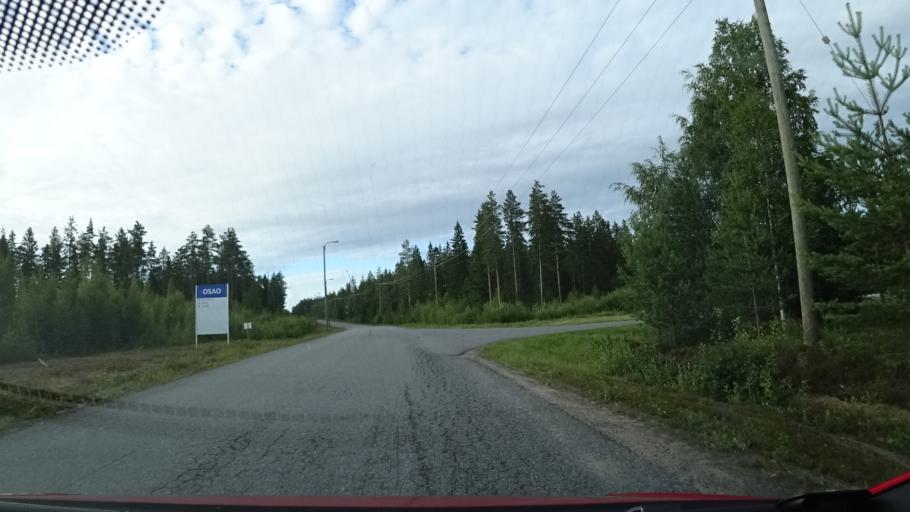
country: FI
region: Northern Ostrobothnia
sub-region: Oulu
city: Haukipudas
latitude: 65.1971
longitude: 25.4133
